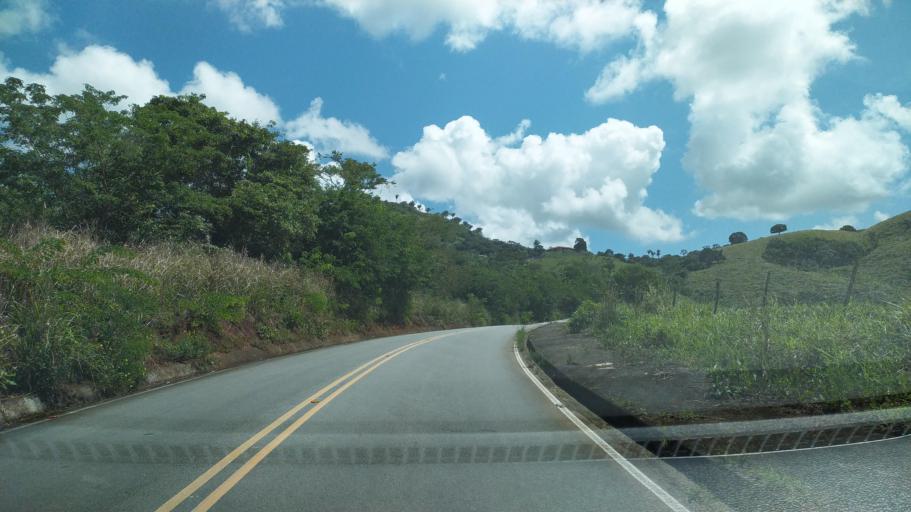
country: BR
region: Alagoas
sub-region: Uniao Dos Palmares
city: Uniao dos Palmares
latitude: -9.1686
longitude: -36.0624
